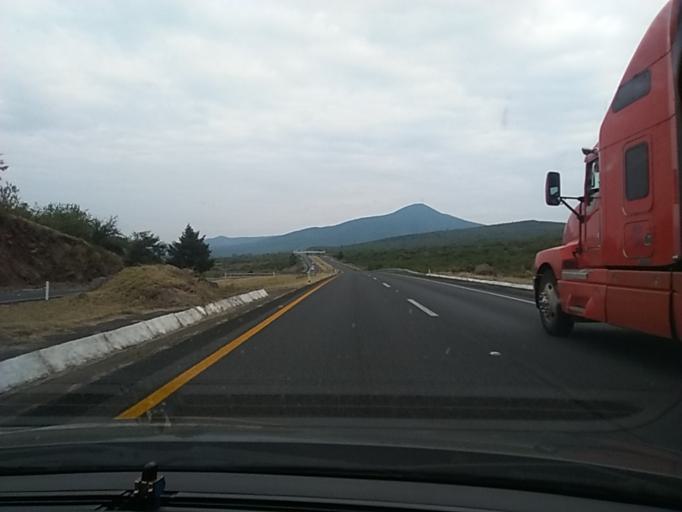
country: MX
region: Michoacan
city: Panindicuaro de la Reforma
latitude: 19.9861
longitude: -101.7952
